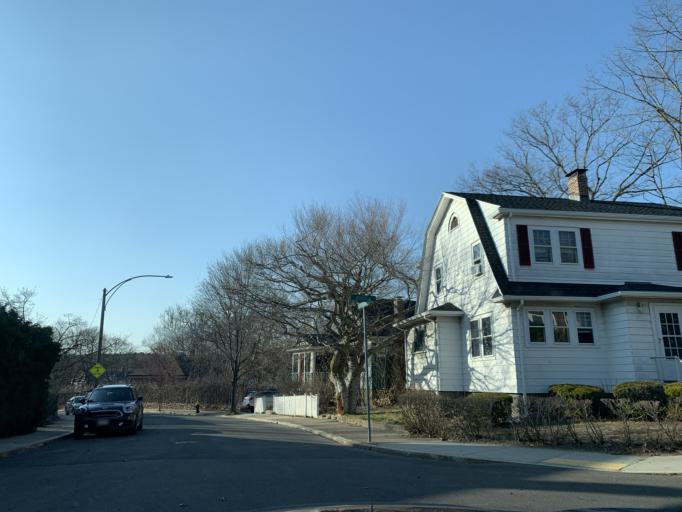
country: US
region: Massachusetts
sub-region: Suffolk County
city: Jamaica Plain
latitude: 42.2915
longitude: -71.1145
